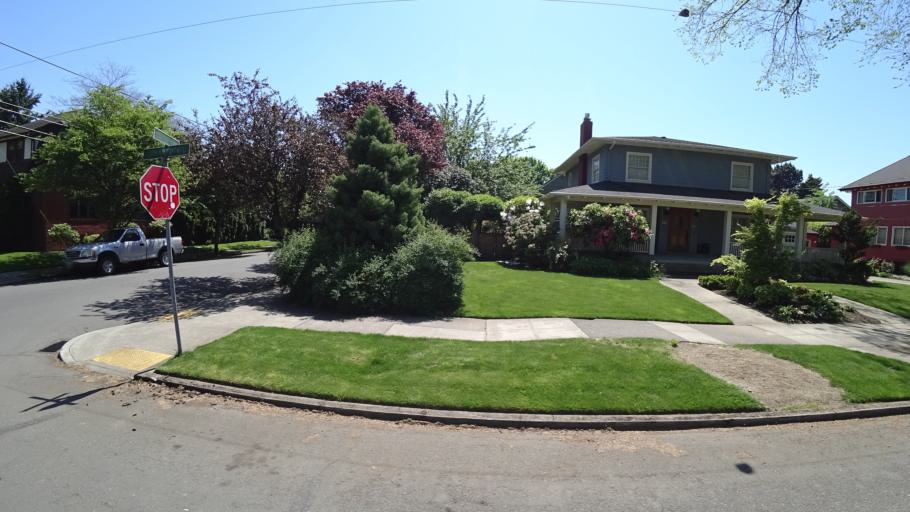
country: US
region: Oregon
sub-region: Multnomah County
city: Portland
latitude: 45.5364
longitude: -122.6382
